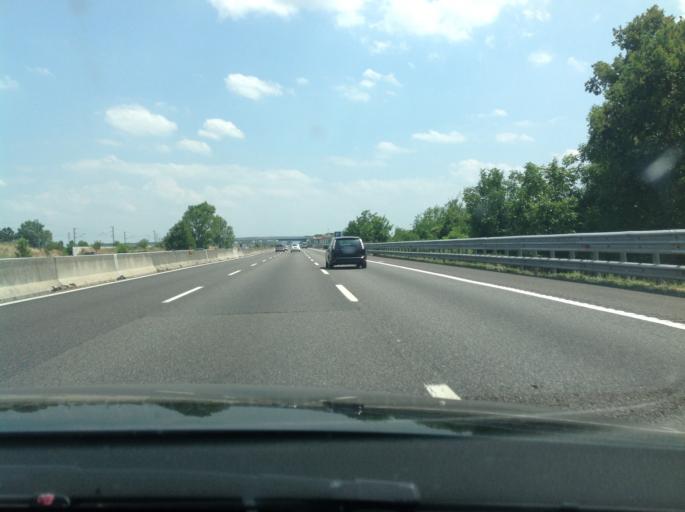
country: IT
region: Emilia-Romagna
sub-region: Provincia di Piacenza
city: Alseno
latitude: 44.9384
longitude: 9.9618
